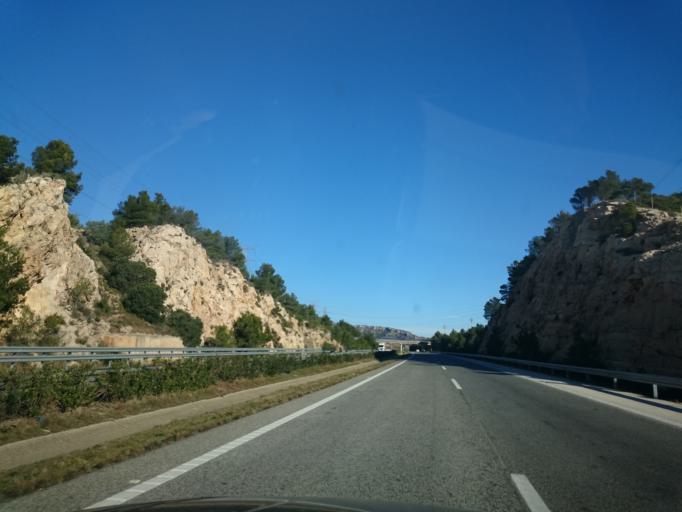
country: ES
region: Catalonia
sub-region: Provincia de Tarragona
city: l'Ametlla de Mar
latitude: 40.9695
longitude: 0.8775
